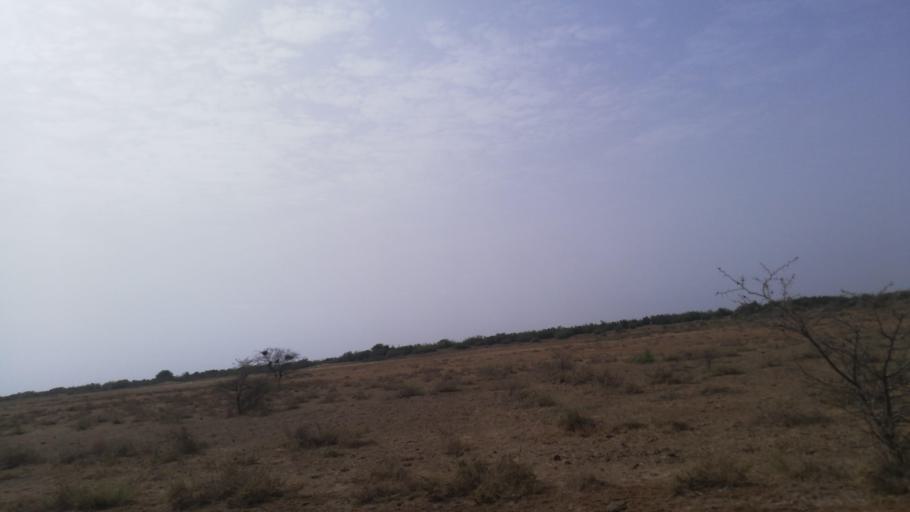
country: SN
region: Saint-Louis
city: Rosso
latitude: 16.3732
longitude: -16.1956
